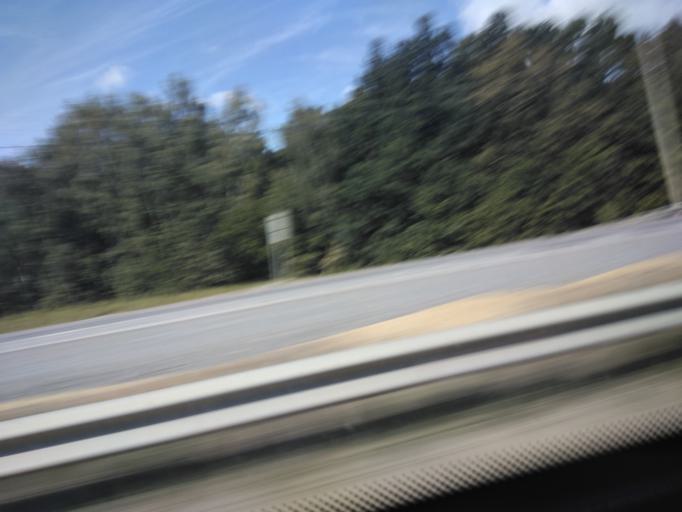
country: RU
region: Tula
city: Zaokskiy
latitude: 54.5884
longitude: 37.5025
